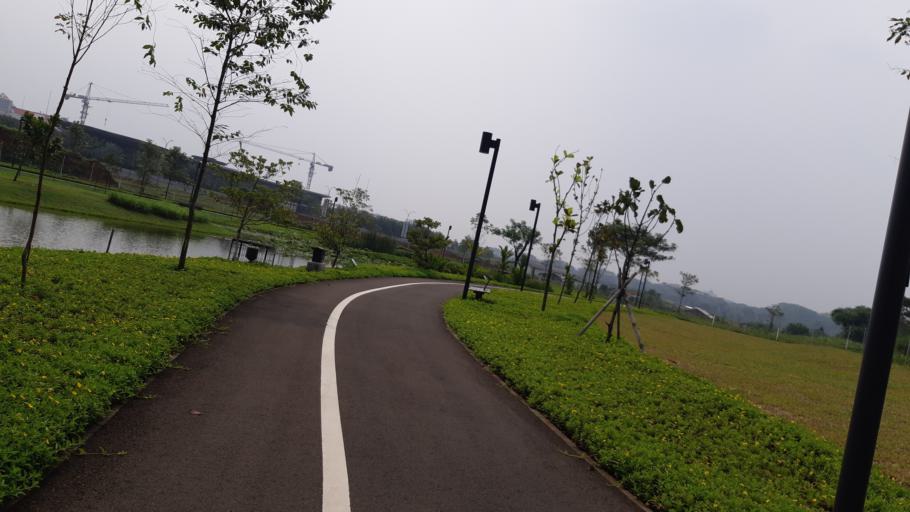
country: ID
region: West Java
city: Serpong
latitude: -6.2938
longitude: 106.6533
